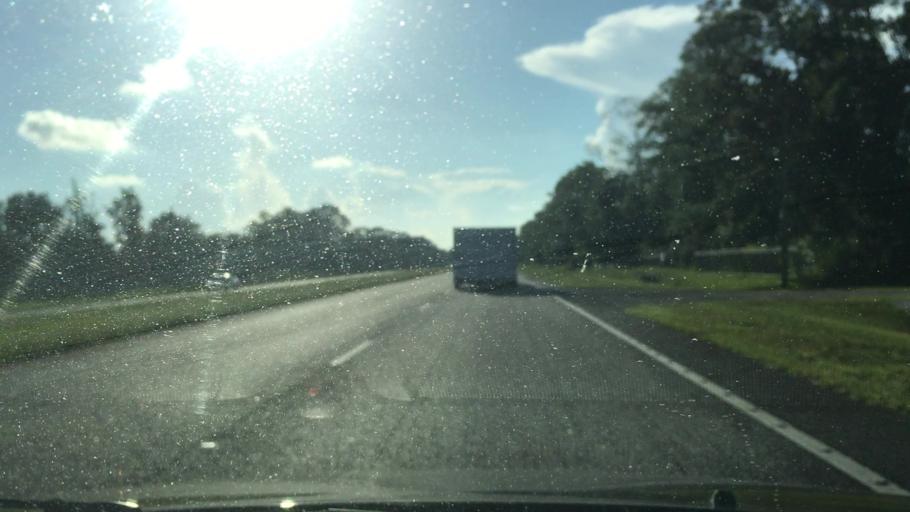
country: US
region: Florida
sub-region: Orange County
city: Christmas
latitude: 28.5369
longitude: -81.0081
